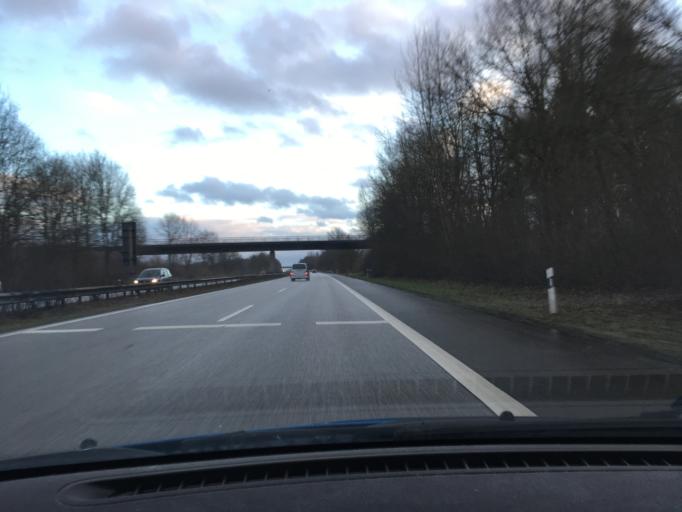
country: DE
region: Schleswig-Holstein
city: Kummerfeld
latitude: 53.6949
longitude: 9.7799
